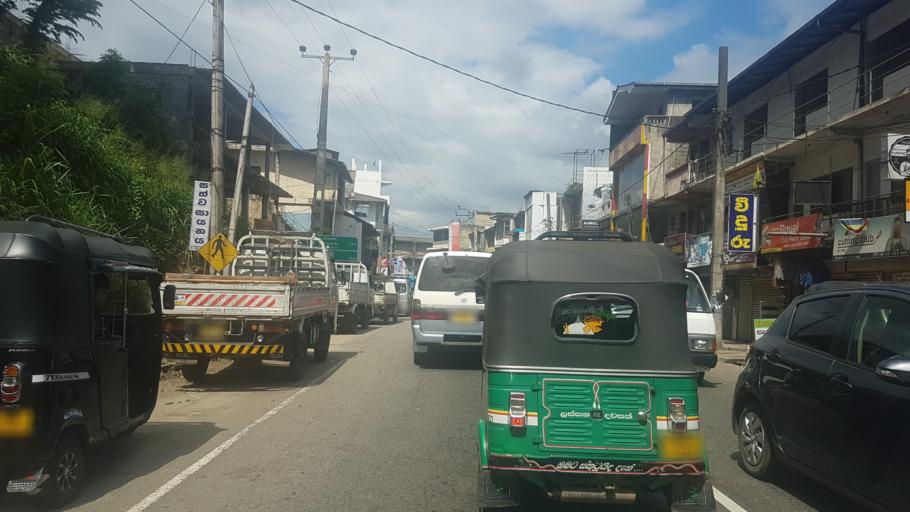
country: LK
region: Central
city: Gampola
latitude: 7.2137
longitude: 80.5985
